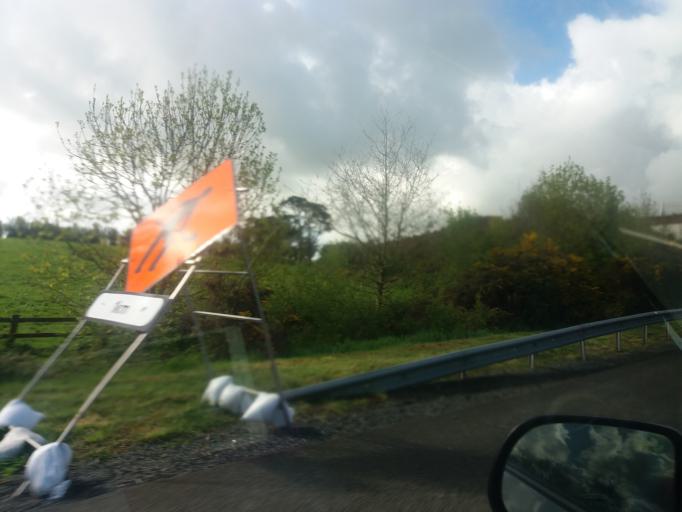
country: IE
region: Leinster
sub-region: Loch Garman
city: Gorey
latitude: 52.6392
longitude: -6.3416
